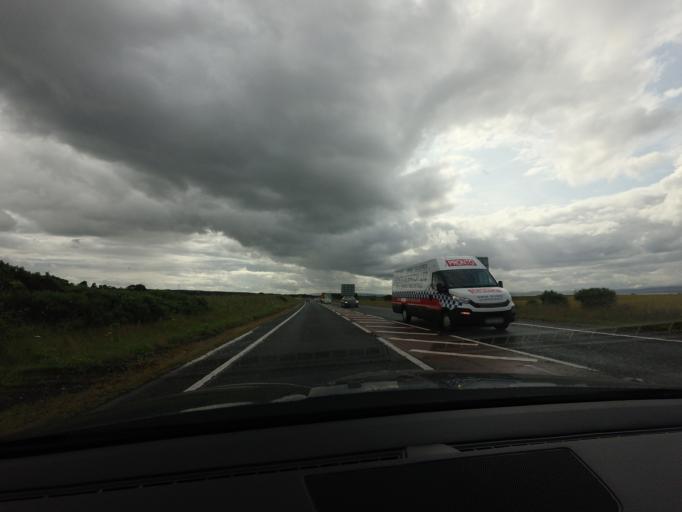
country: GB
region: Scotland
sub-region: Highland
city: Nairn
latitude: 57.5442
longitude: -4.0051
